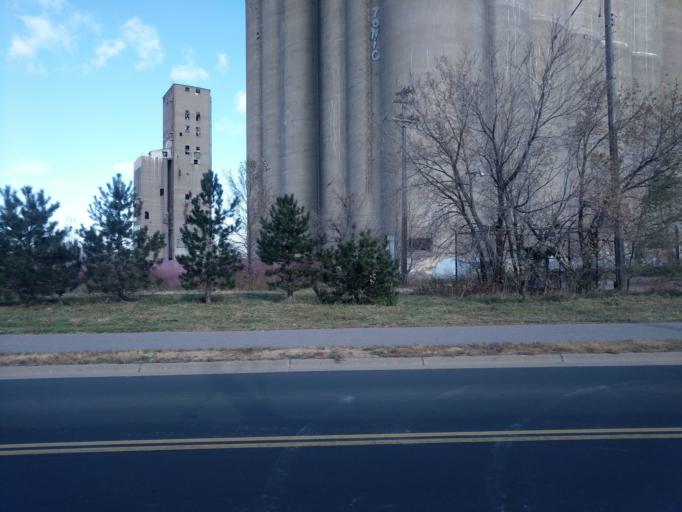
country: US
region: Minnesota
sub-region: Ramsey County
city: Lauderdale
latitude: 44.9732
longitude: -93.2156
